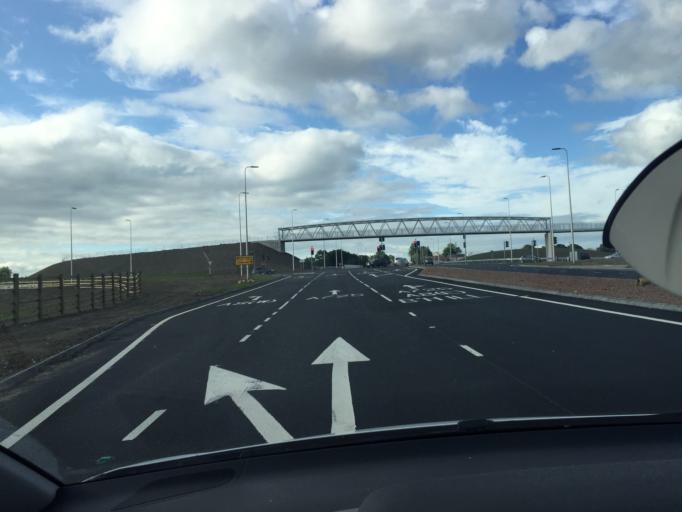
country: GB
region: Scotland
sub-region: North Lanarkshire
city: Coatbridge
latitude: 55.8391
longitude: -4.0248
